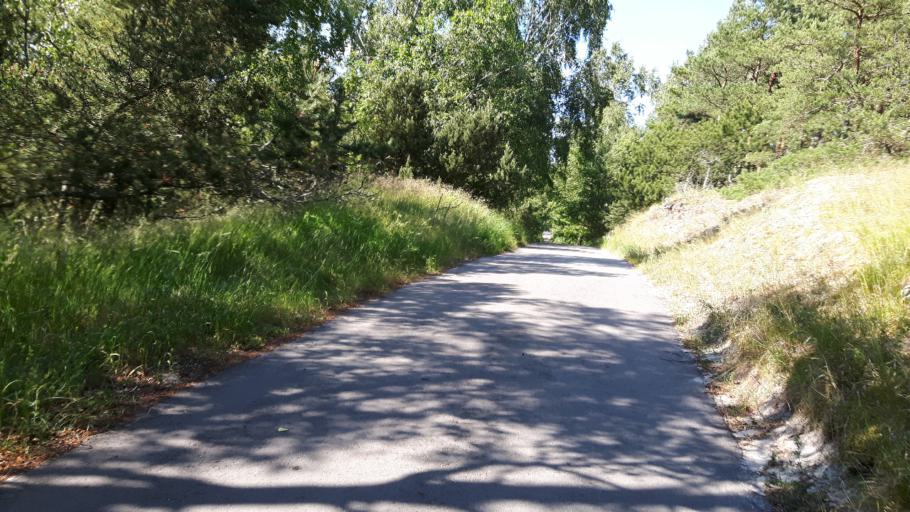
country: LT
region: Klaipedos apskritis
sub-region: Klaipeda
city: Klaipeda
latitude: 55.6874
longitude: 21.1037
